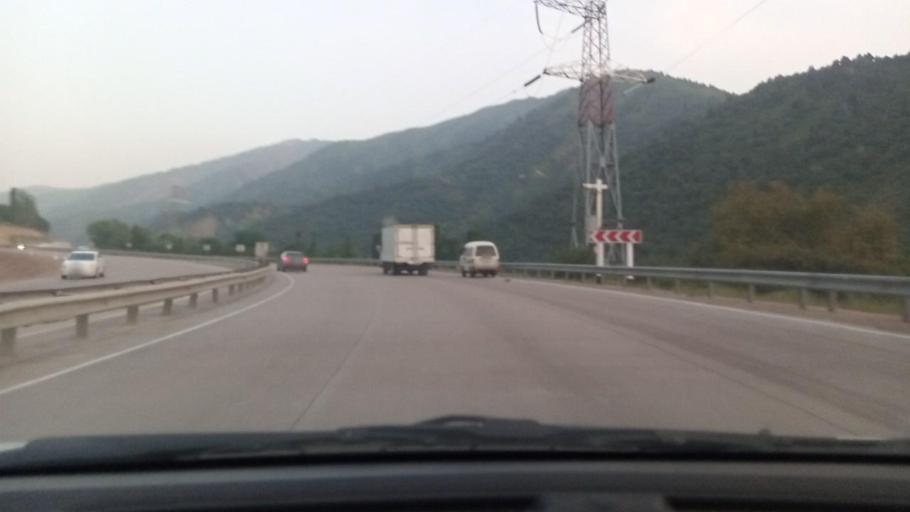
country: UZ
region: Toshkent
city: Angren
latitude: 41.1462
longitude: 70.4461
